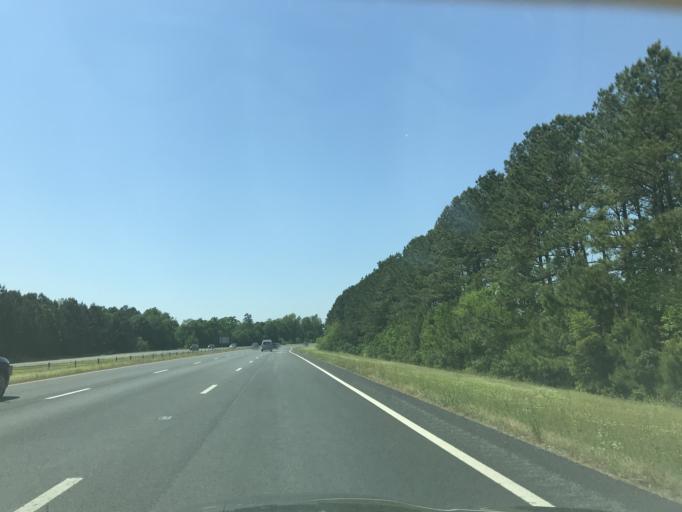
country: US
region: North Carolina
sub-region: Johnston County
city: Benson
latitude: 35.3313
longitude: -78.4538
